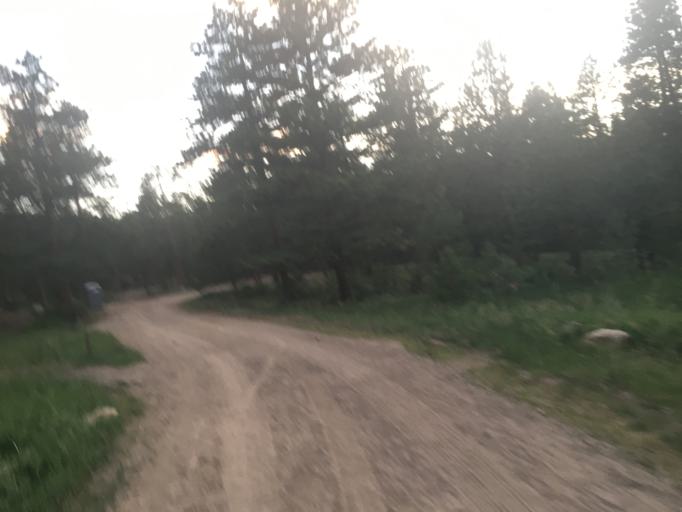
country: US
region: Colorado
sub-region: Larimer County
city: Estes Park
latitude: 40.3468
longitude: -105.5727
